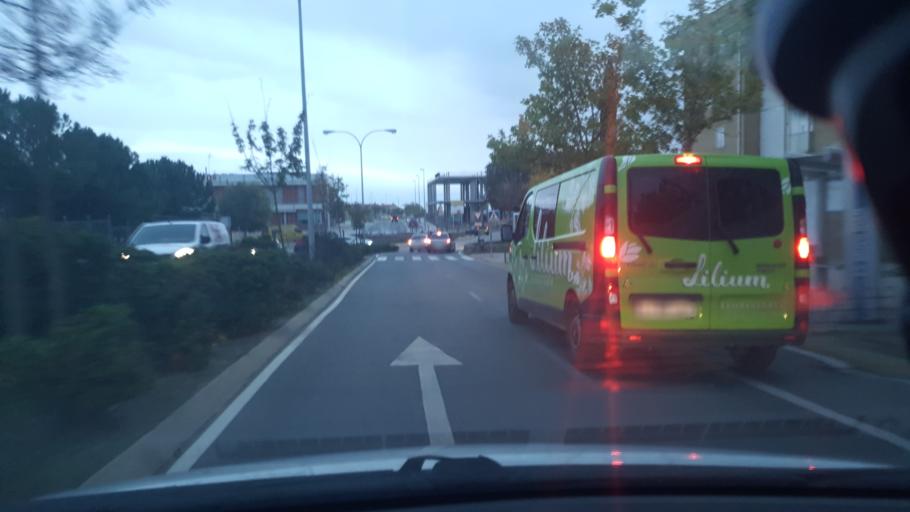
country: ES
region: Castille and Leon
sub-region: Provincia de Segovia
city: Segovia
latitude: 40.9333
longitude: -4.1033
